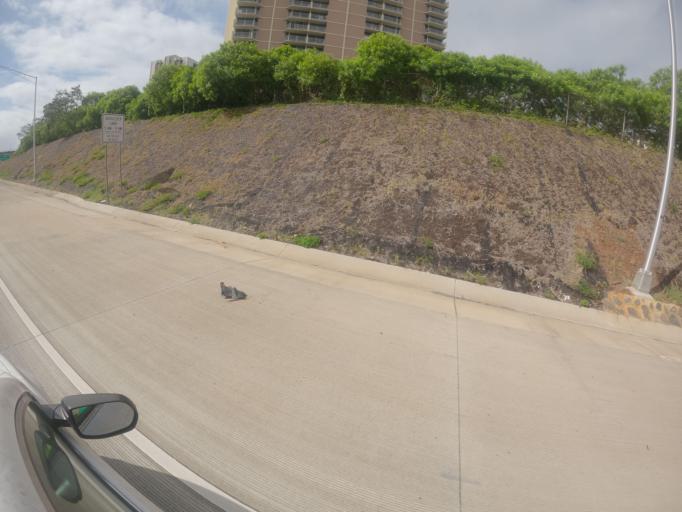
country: US
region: Hawaii
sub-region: Honolulu County
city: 'Aiea
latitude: 21.3865
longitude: -157.9358
